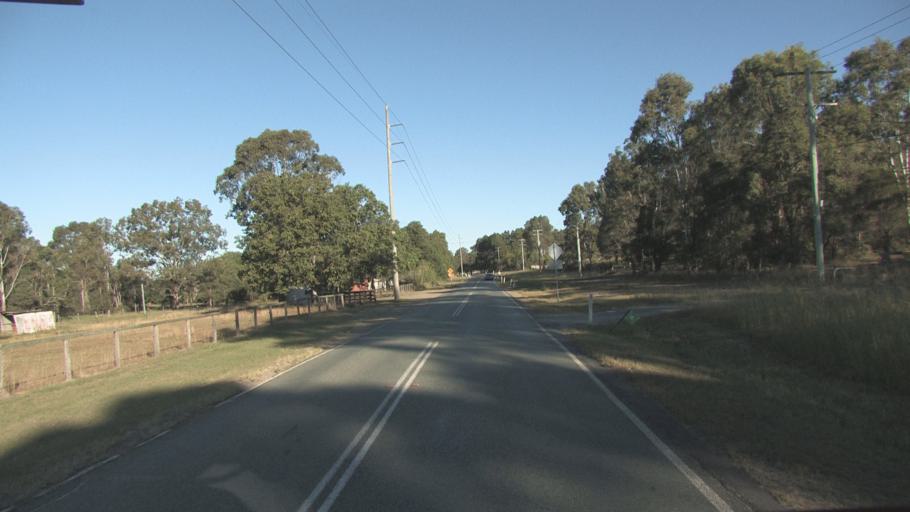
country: AU
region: Queensland
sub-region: Logan
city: Chambers Flat
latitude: -27.7417
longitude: 153.0873
